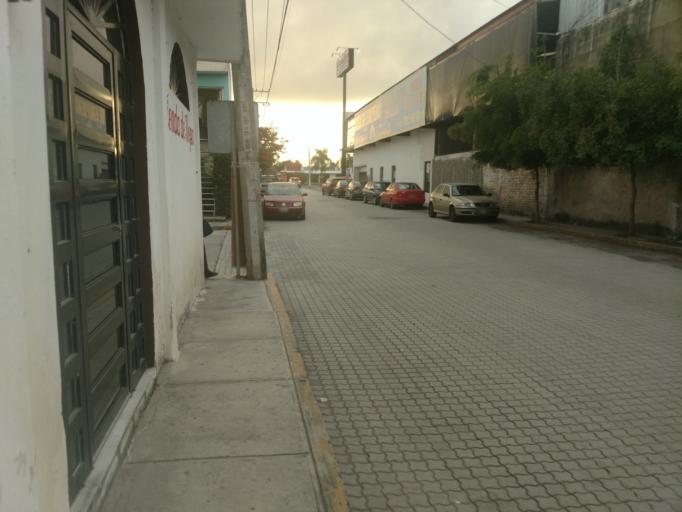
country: MX
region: Nayarit
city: Xalisco
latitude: 21.4746
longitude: -104.8571
